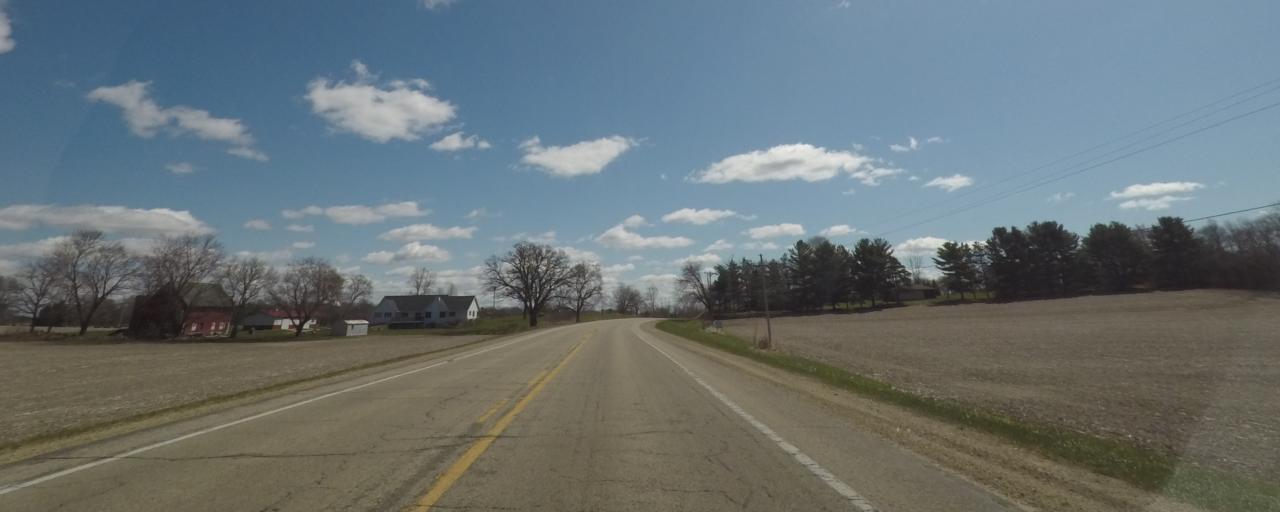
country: US
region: Wisconsin
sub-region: Dane County
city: Cottage Grove
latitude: 43.0915
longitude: -89.1823
